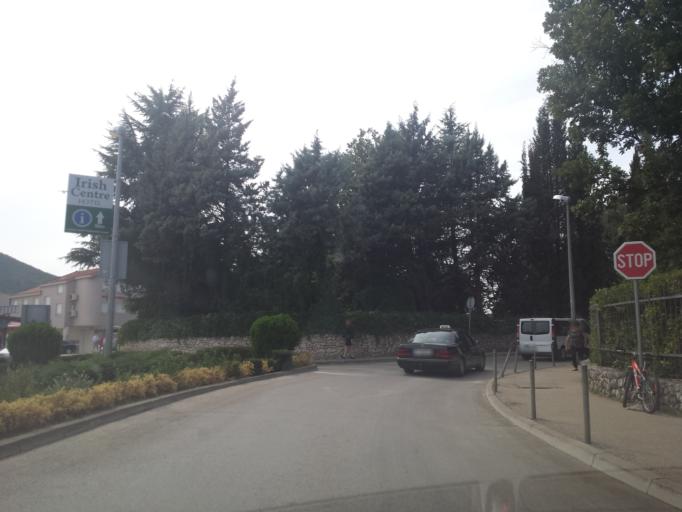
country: BA
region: Federation of Bosnia and Herzegovina
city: Citluk
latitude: 43.1901
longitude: 17.6801
